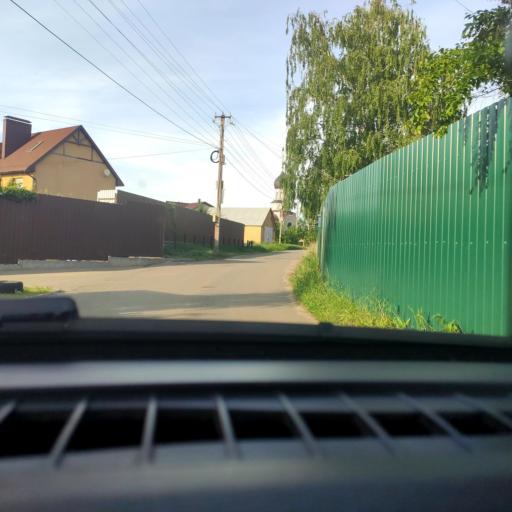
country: RU
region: Voronezj
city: Podgornoye
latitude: 51.7894
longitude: 39.1376
